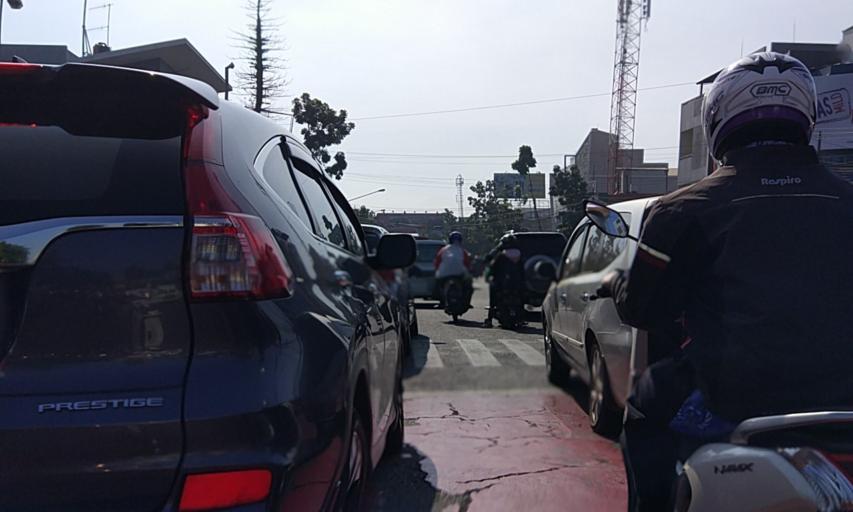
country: ID
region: West Java
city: Bandung
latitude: -6.9135
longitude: 107.6340
